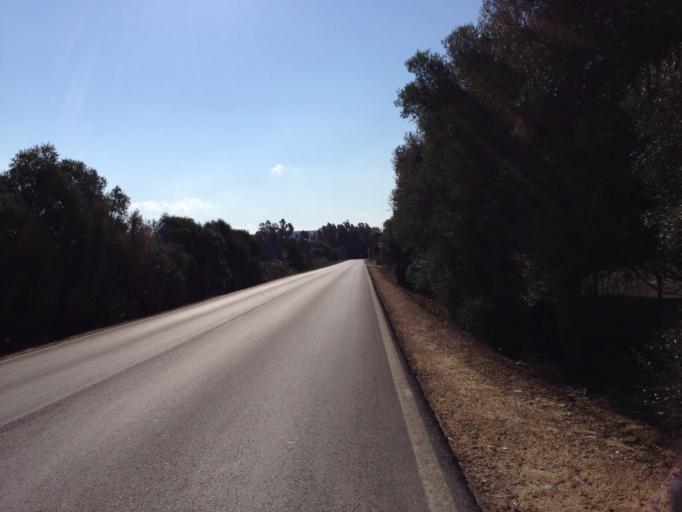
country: ES
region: Andalusia
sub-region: Provincia de Cadiz
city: Vejer de la Frontera
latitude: 36.2137
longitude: -6.0351
